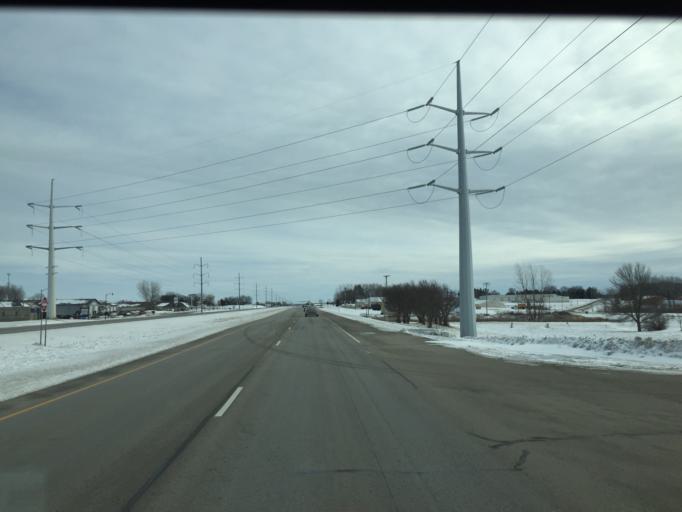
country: US
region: Minnesota
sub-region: Olmsted County
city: Byron
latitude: 44.0286
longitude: -92.6384
